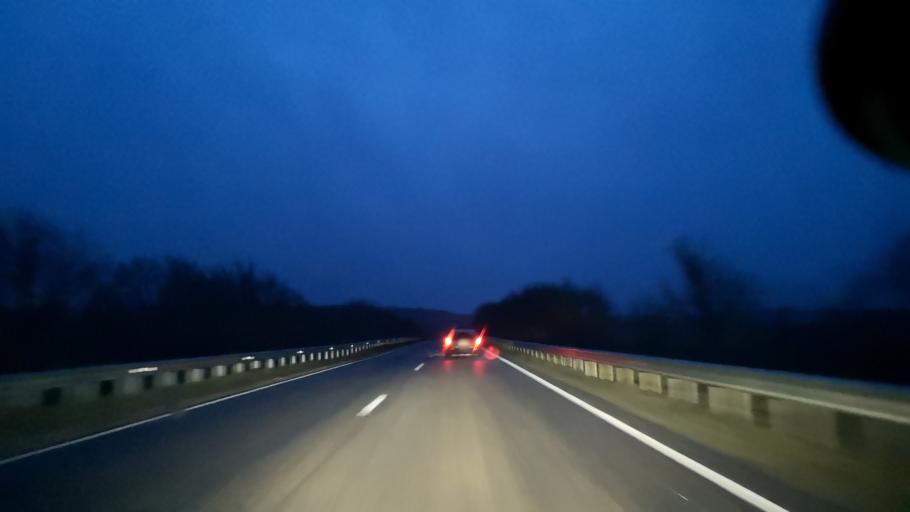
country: MD
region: Orhei
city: Orhei
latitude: 47.4916
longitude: 28.7919
